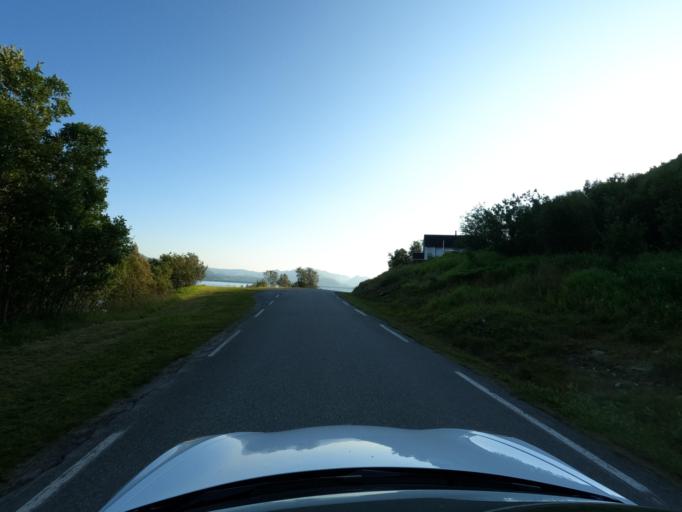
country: NO
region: Nordland
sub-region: Ballangen
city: Ballangen
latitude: 68.4623
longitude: 16.7676
